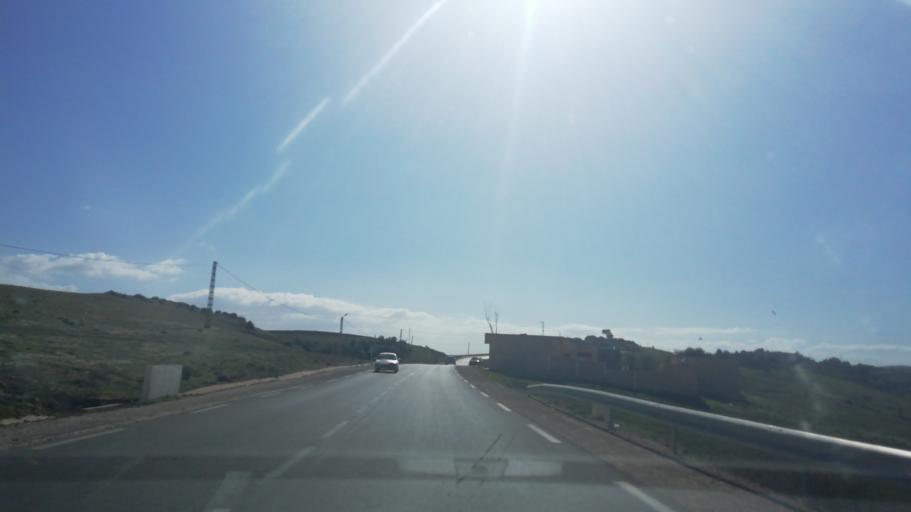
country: DZ
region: Relizane
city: Djidiouia
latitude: 36.0899
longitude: 0.5154
